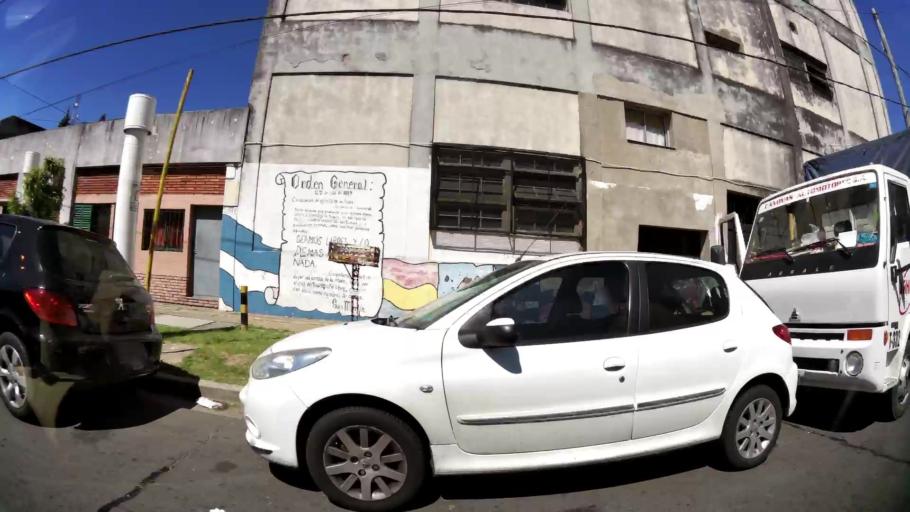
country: AR
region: Buenos Aires
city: Caseros
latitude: -34.5878
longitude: -58.5508
